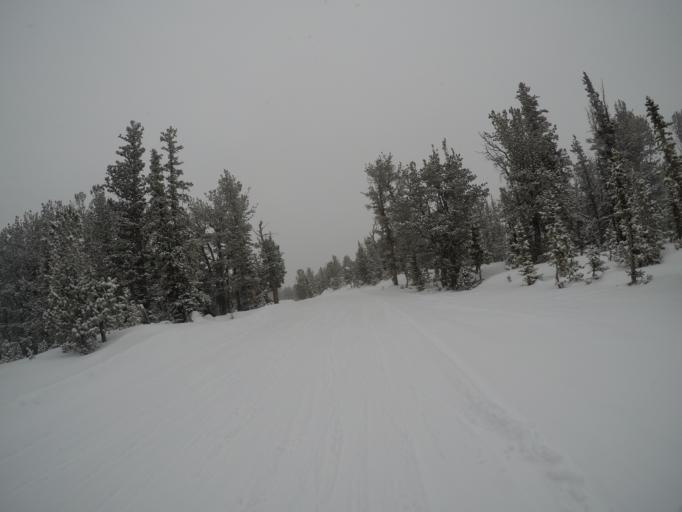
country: US
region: Montana
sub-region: Carbon County
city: Red Lodge
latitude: 45.1831
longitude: -109.3575
